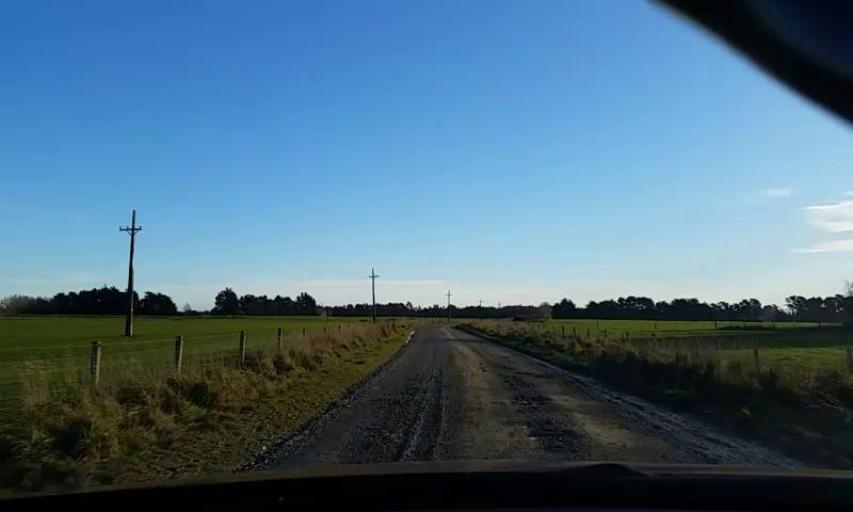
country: NZ
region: Southland
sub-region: Invercargill City
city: Invercargill
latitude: -46.2913
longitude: 168.4289
